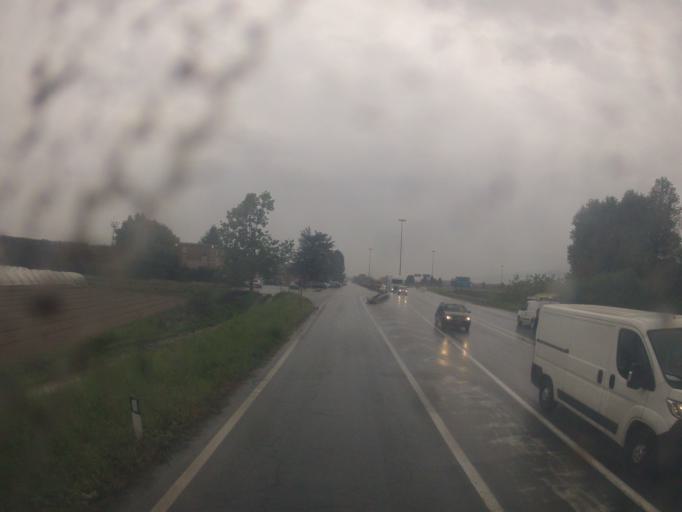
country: IT
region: Piedmont
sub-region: Provincia di Torino
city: La Loggia
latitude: 44.9383
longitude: 7.6709
